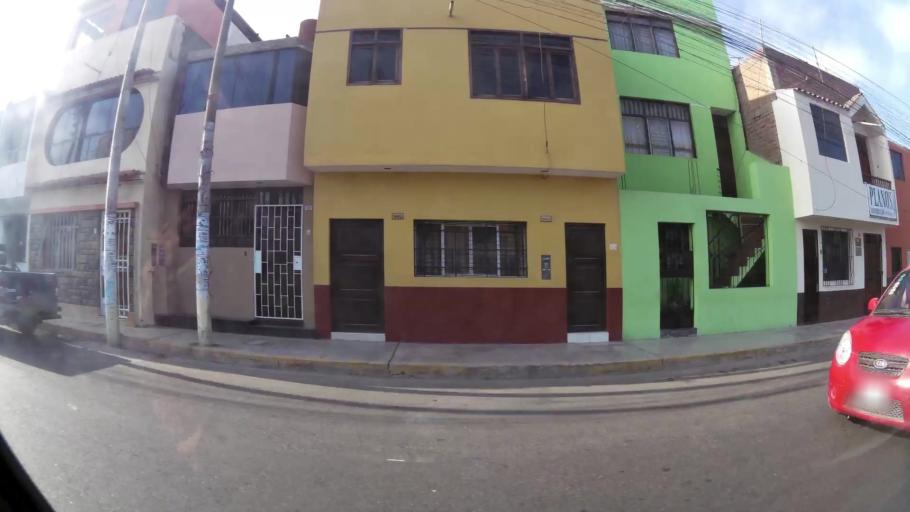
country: PE
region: La Libertad
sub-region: Provincia de Trujillo
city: Trujillo
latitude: -8.1011
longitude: -79.0461
